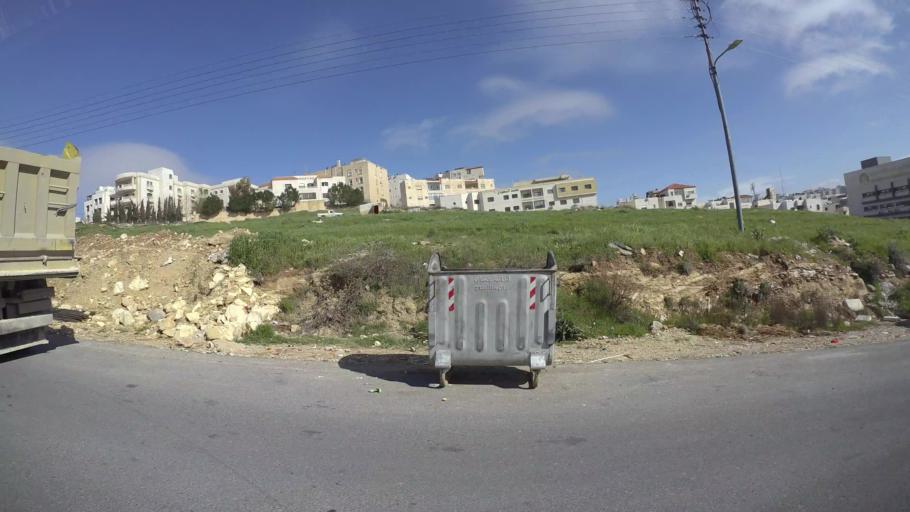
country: JO
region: Amman
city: Al Jubayhah
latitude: 32.0013
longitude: 35.8440
